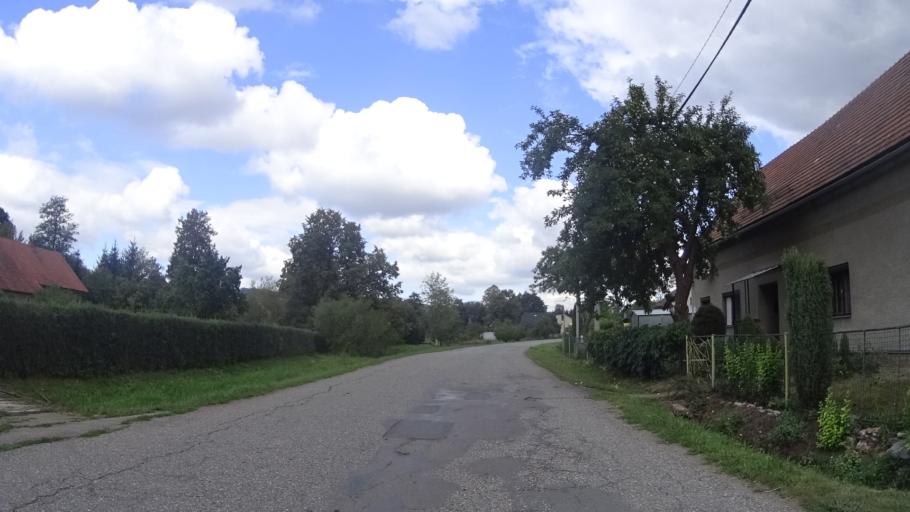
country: CZ
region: Pardubicky
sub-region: Okres Usti nad Orlici
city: Lanskroun
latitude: 49.9214
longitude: 16.5560
